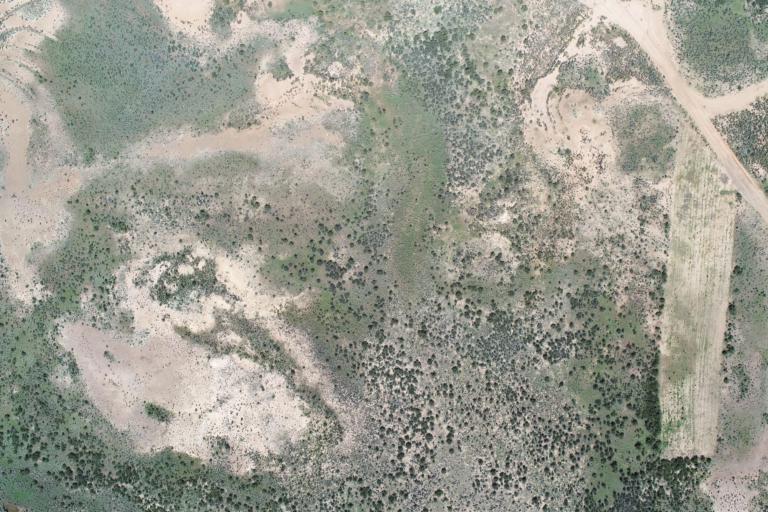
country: BO
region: La Paz
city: Curahuara de Carangas
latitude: -17.2926
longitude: -68.5135
